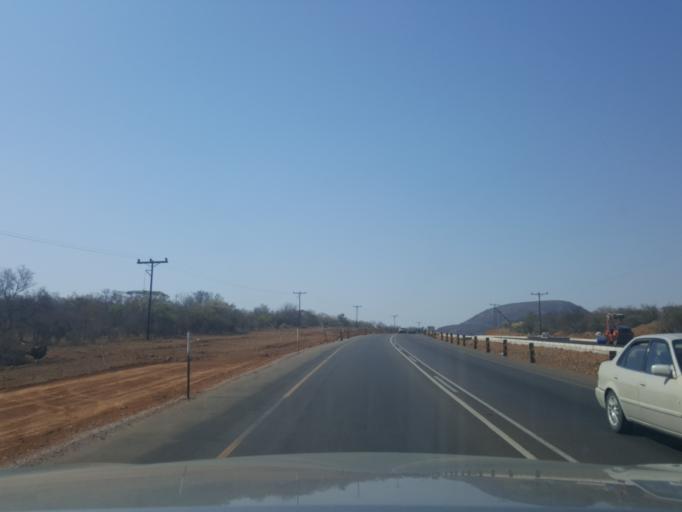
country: BW
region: Kweneng
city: Gabane
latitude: -24.7506
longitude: 25.8287
